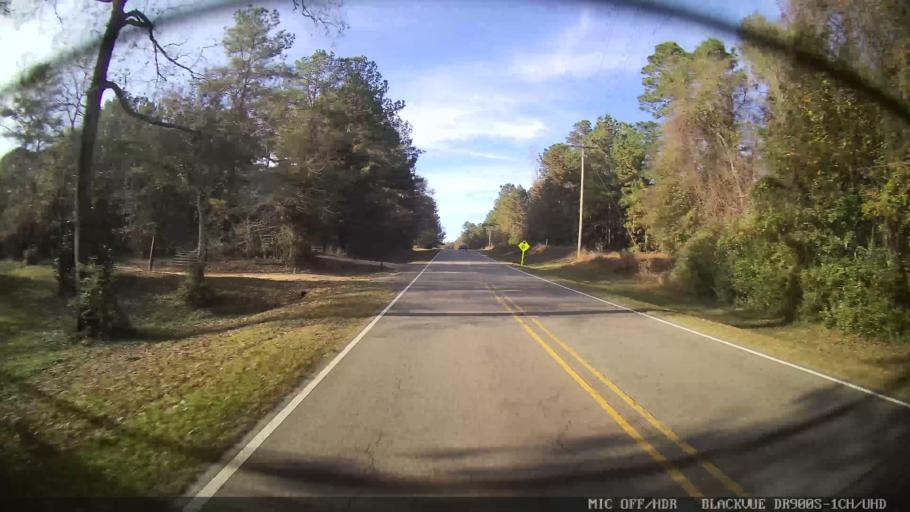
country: US
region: Mississippi
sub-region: Forrest County
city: Hattiesburg
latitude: 31.2110
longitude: -89.2948
